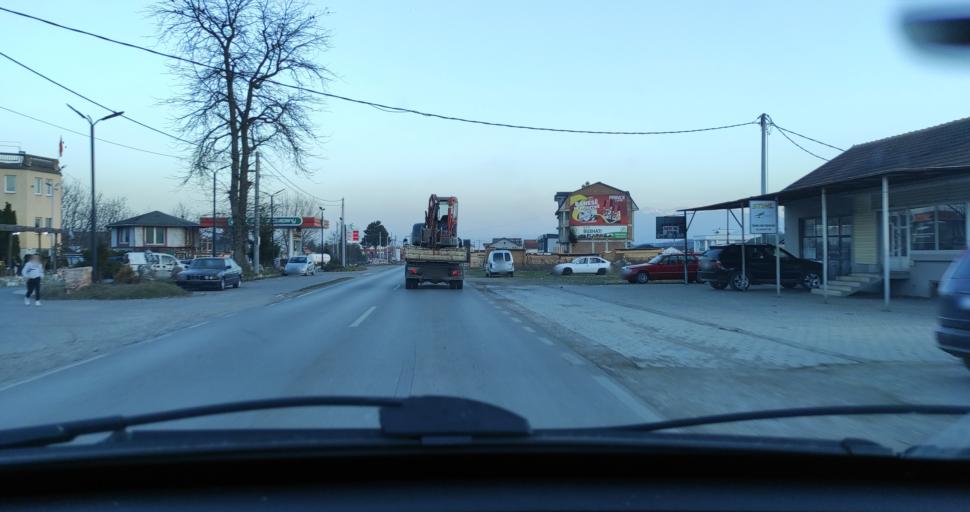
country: XK
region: Gjakova
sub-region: Komuna e Gjakoves
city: Gjakove
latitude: 42.4112
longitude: 20.4028
